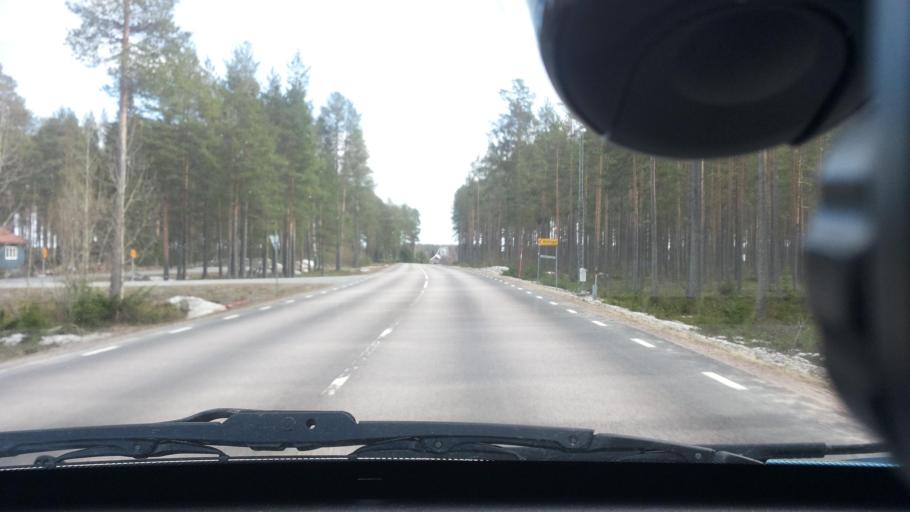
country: SE
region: Norrbotten
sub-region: Lulea Kommun
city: Sodra Sunderbyn
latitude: 65.6278
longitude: 21.9284
